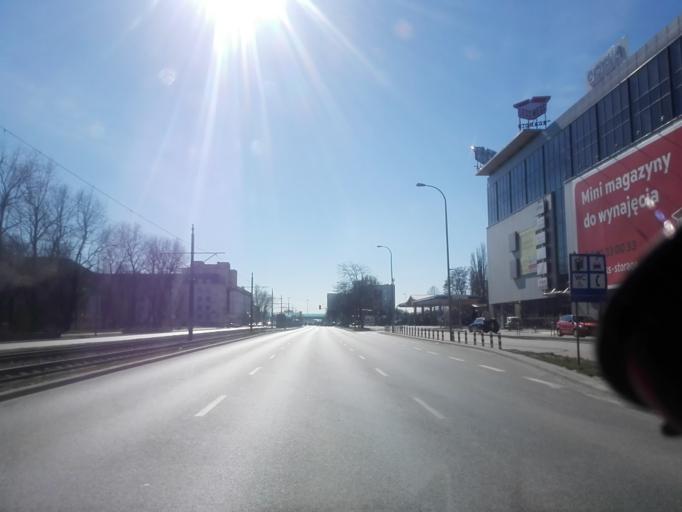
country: PL
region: Masovian Voivodeship
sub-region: Warszawa
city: Wlochy
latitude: 52.1947
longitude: 20.9619
